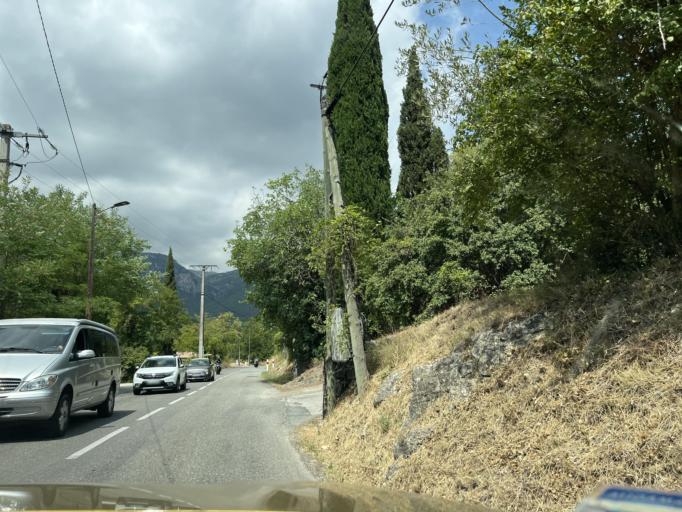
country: FR
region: Provence-Alpes-Cote d'Azur
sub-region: Departement des Alpes-Maritimes
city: Le Rouret
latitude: 43.7020
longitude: 7.0036
